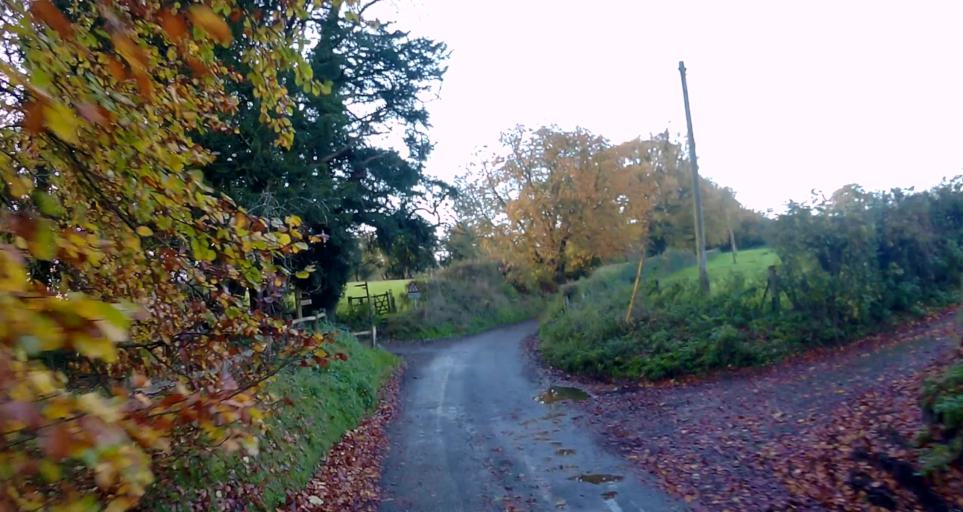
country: GB
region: England
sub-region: Hampshire
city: Basingstoke
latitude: 51.2091
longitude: -1.0872
